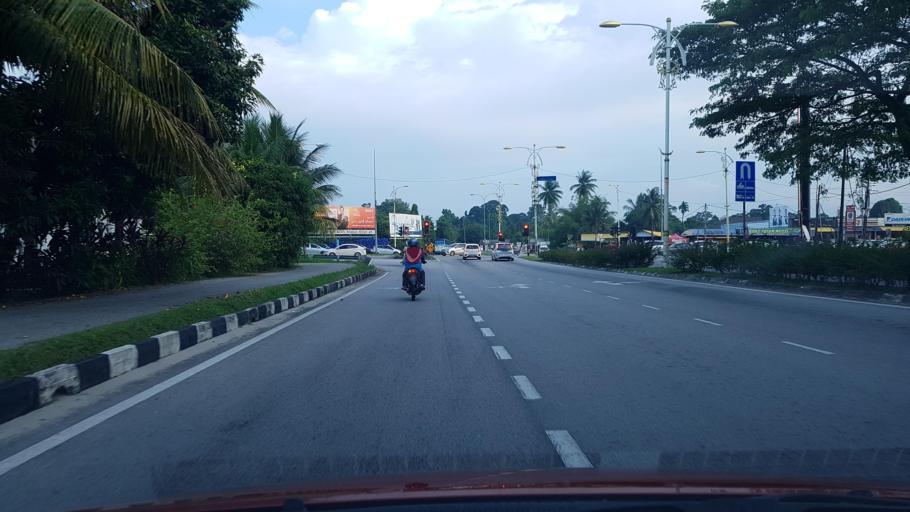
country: MY
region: Terengganu
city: Kuala Terengganu
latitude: 5.3404
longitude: 103.1020
